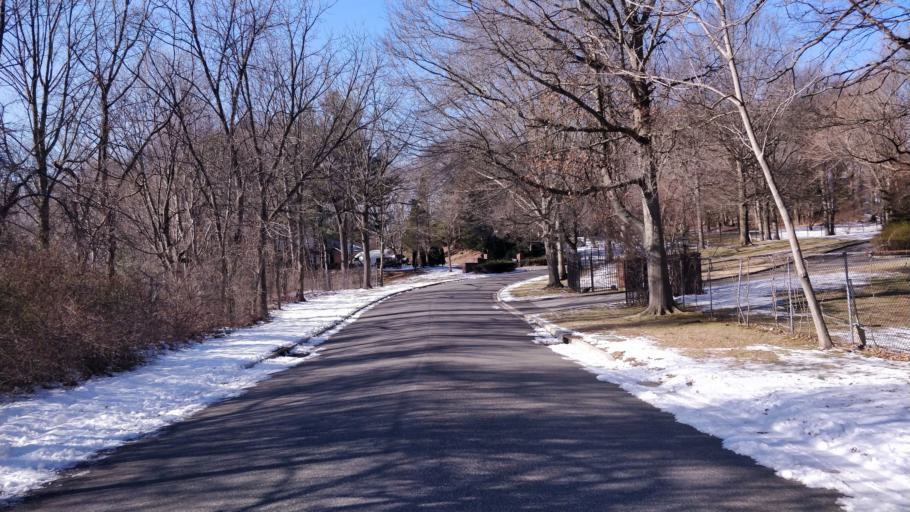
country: US
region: New York
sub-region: Nassau County
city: Old Westbury
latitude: 40.7849
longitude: -73.5896
